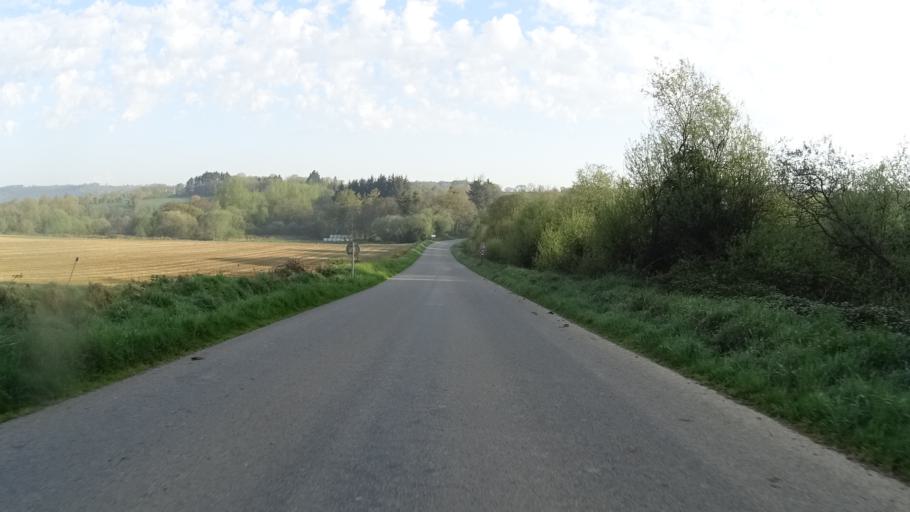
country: FR
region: Brittany
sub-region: Departement du Finistere
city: Sizun
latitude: 48.4337
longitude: -4.0718
